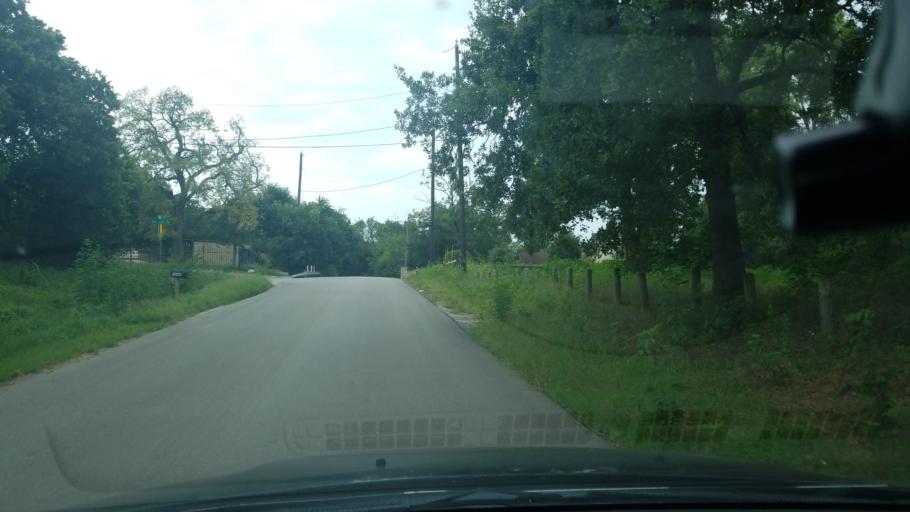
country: US
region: Texas
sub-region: Dallas County
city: Balch Springs
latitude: 32.7300
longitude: -96.6619
